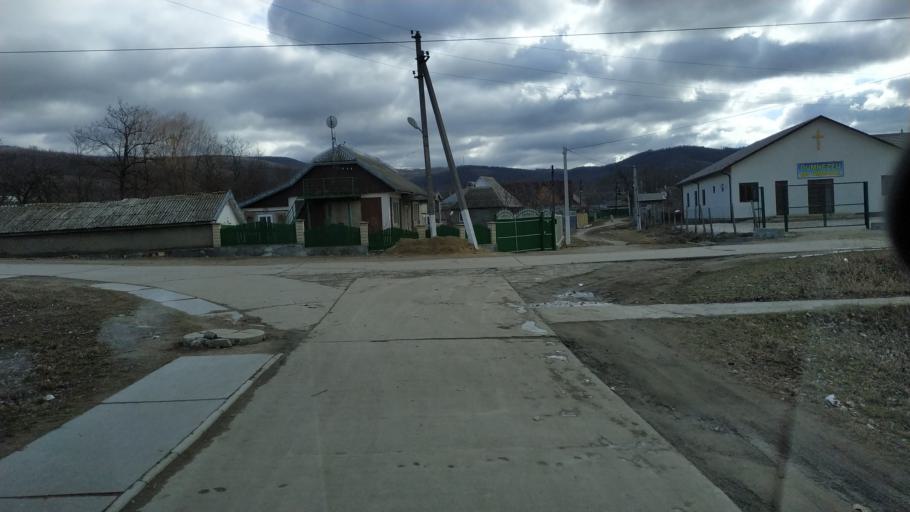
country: MD
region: Stinga Nistrului
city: Bucovat
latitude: 47.1338
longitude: 28.3857
